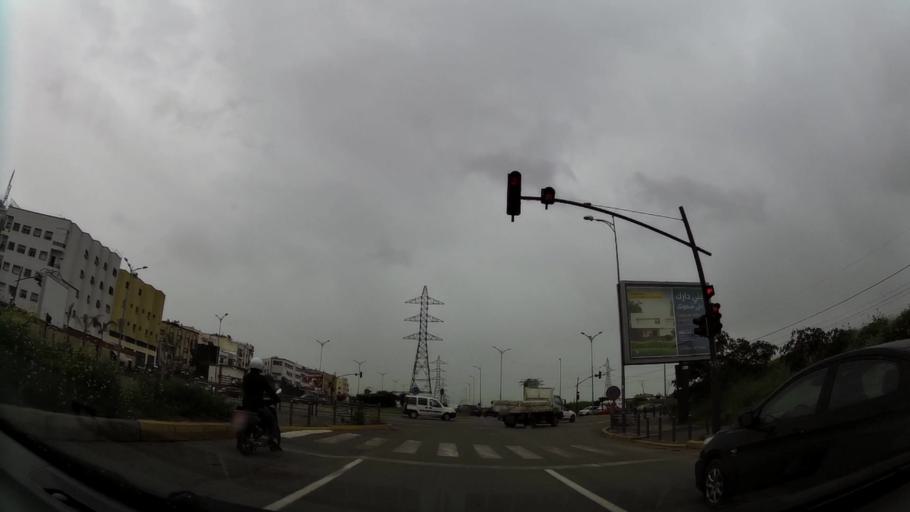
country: MA
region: Grand Casablanca
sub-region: Casablanca
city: Casablanca
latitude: 33.5322
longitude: -7.6174
